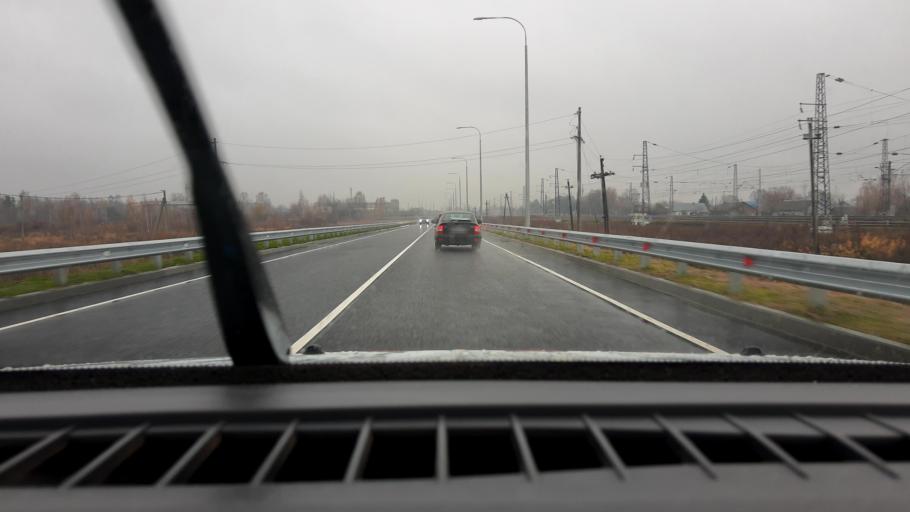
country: RU
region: Nizjnij Novgorod
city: Neklyudovo
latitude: 56.4120
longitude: 43.9835
